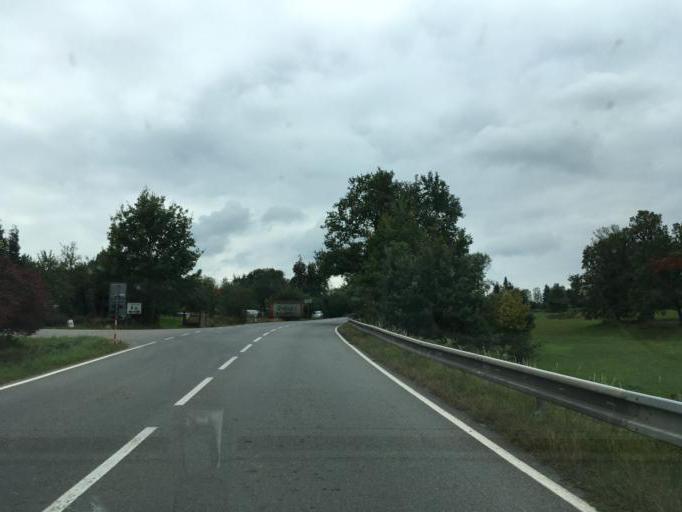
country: CZ
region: Vysocina
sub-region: Okres Pelhrimov
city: Zeliv
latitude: 49.5095
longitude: 15.1790
